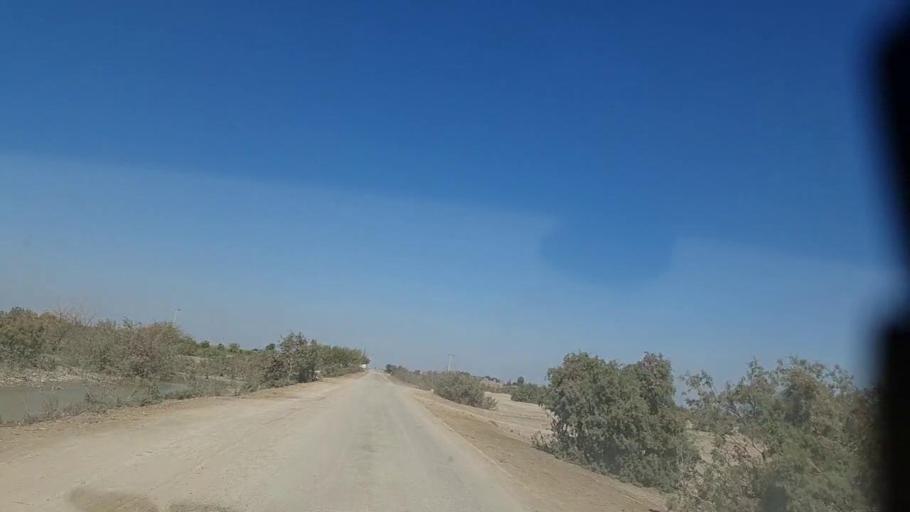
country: PK
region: Sindh
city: Digri
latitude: 25.1846
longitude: 69.0485
